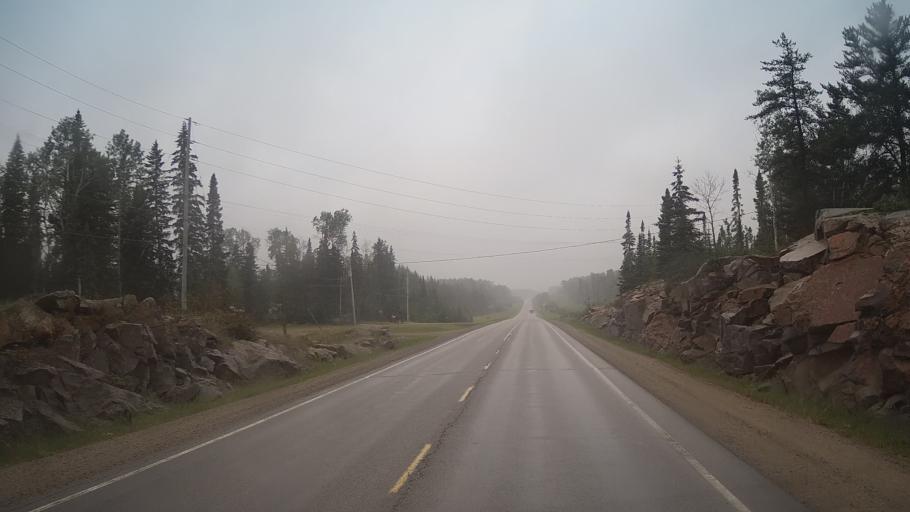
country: CA
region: Ontario
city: Greenstone
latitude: 49.7816
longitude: -86.5813
